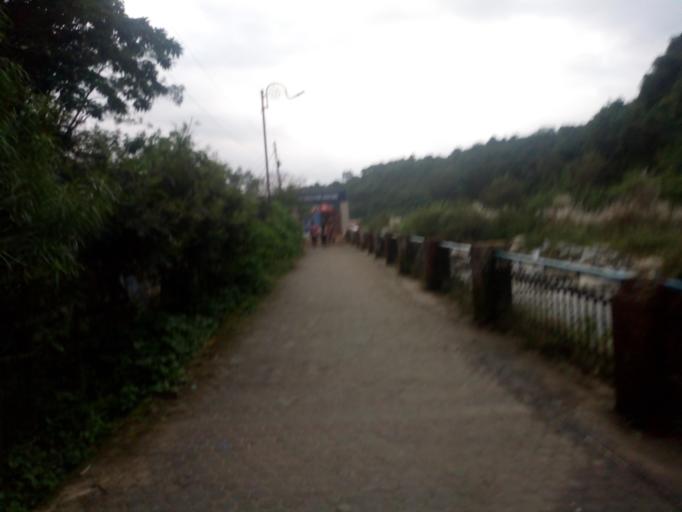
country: IN
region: Uttarakhand
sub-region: Dehradun
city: Dehradun
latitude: 30.3757
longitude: 78.0598
